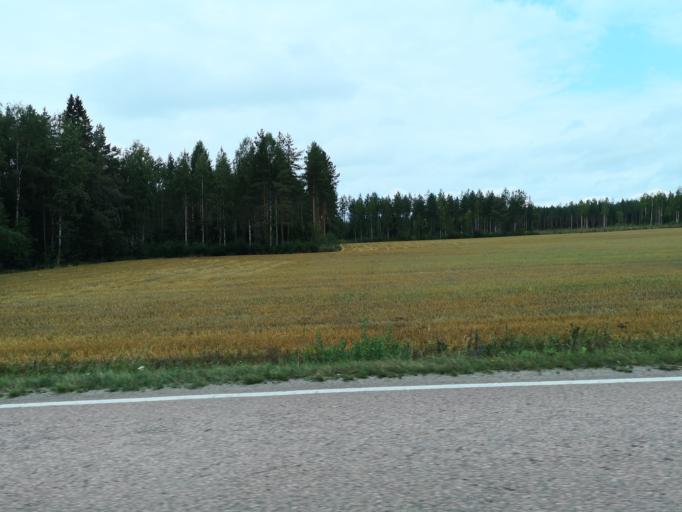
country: FI
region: Central Finland
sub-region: Jyvaeskylae
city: Hankasalmi
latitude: 62.3585
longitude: 26.5066
